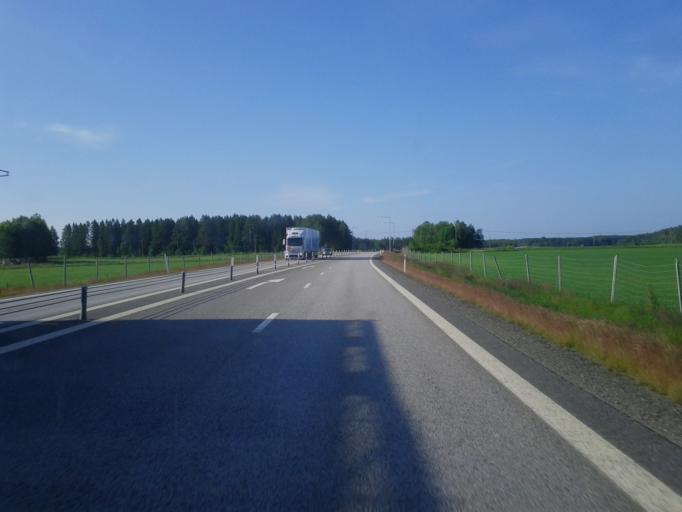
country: SE
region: Vaesterbotten
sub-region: Robertsfors Kommun
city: Robertsfors
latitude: 64.0975
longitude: 20.8699
